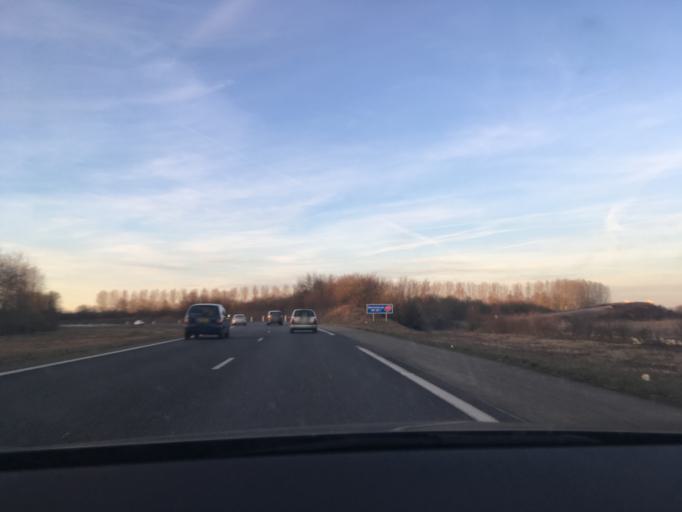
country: FR
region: Ile-de-France
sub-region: Departement de Seine-et-Marne
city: Vert-Saint-Denis
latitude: 48.5877
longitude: 2.6376
